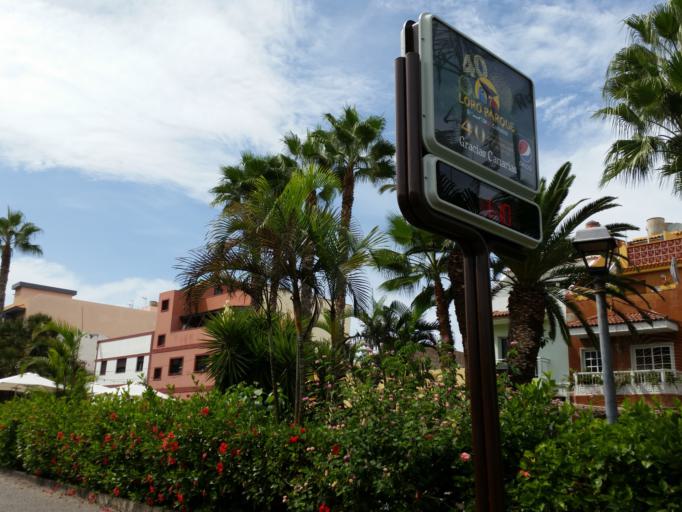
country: ES
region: Canary Islands
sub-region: Provincia de Santa Cruz de Tenerife
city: Puerto de la Cruz
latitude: 28.4093
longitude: -16.5664
